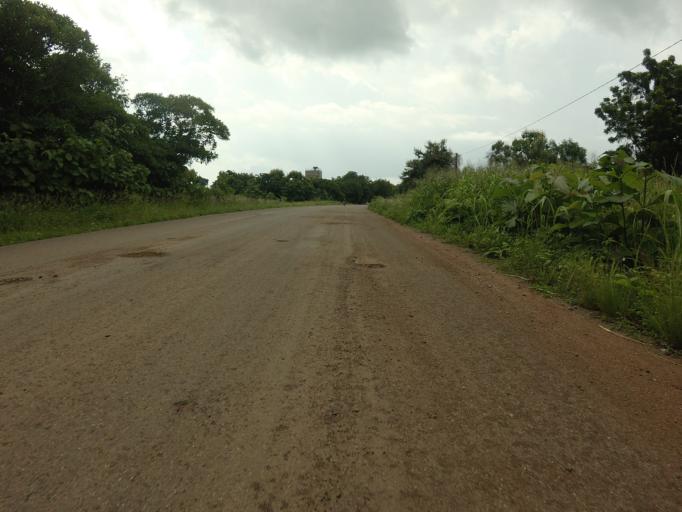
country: GH
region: Volta
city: Kpandu
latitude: 6.9502
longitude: 0.4589
